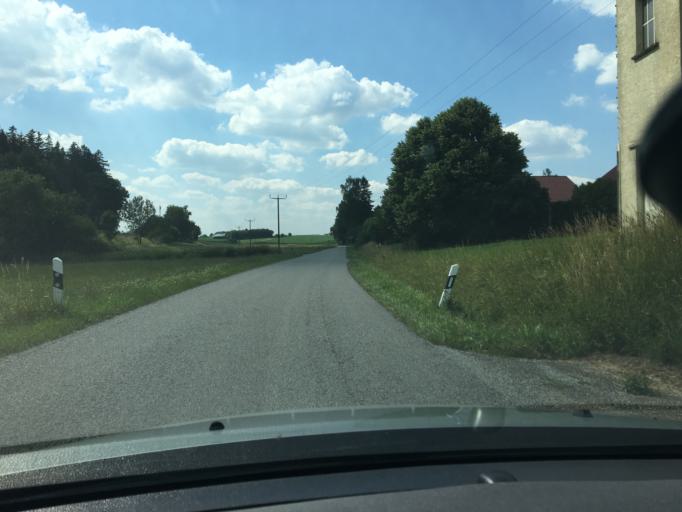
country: DE
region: Bavaria
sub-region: Lower Bavaria
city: Geisenhausen
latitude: 48.4598
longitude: 12.2834
